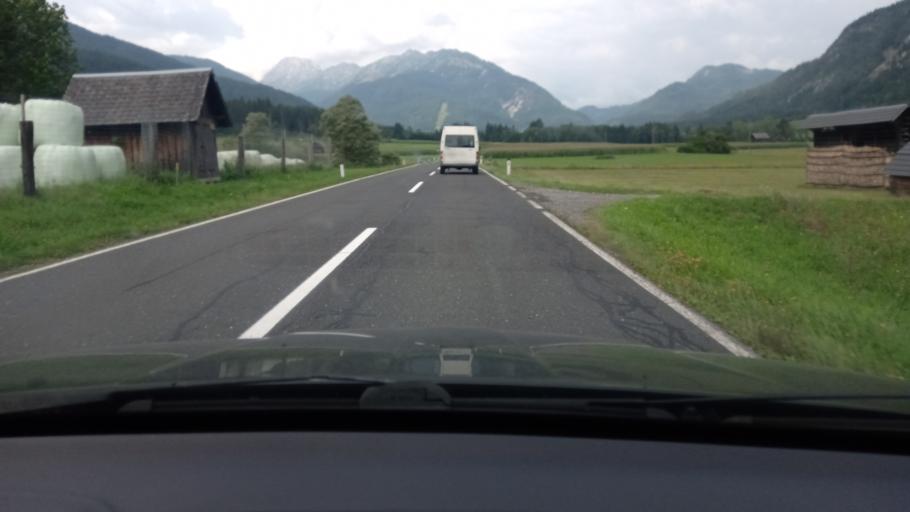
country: AT
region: Carinthia
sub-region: Politischer Bezirk Hermagor
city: Hermagor
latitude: 46.6683
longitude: 13.2943
